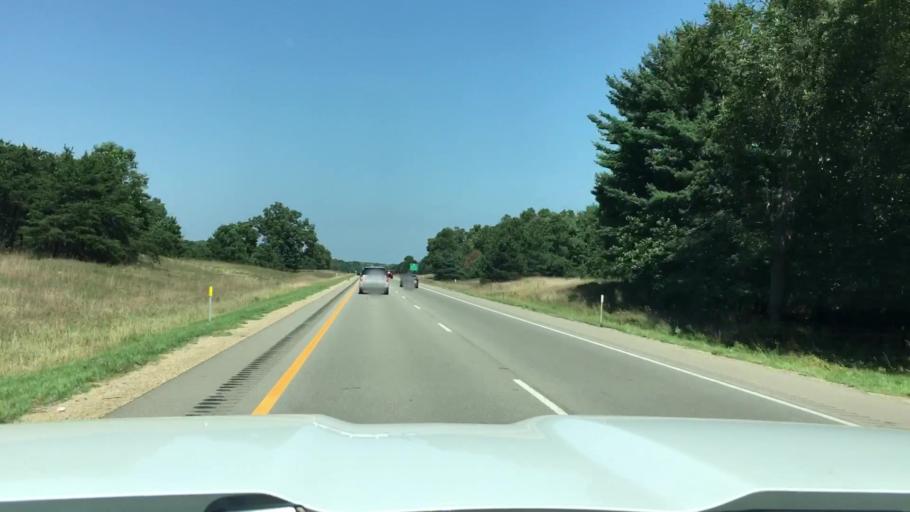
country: US
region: Michigan
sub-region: Kalamazoo County
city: Portage
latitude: 42.1837
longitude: -85.6457
